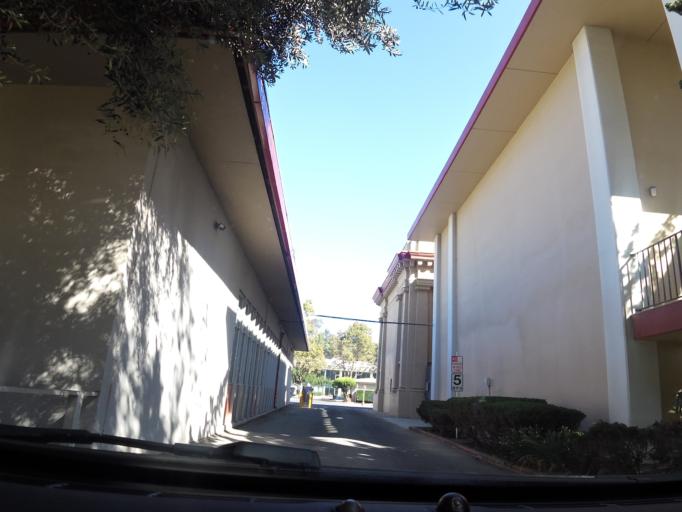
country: US
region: California
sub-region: San Benito County
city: Hollister
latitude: 36.8516
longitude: -121.4048
